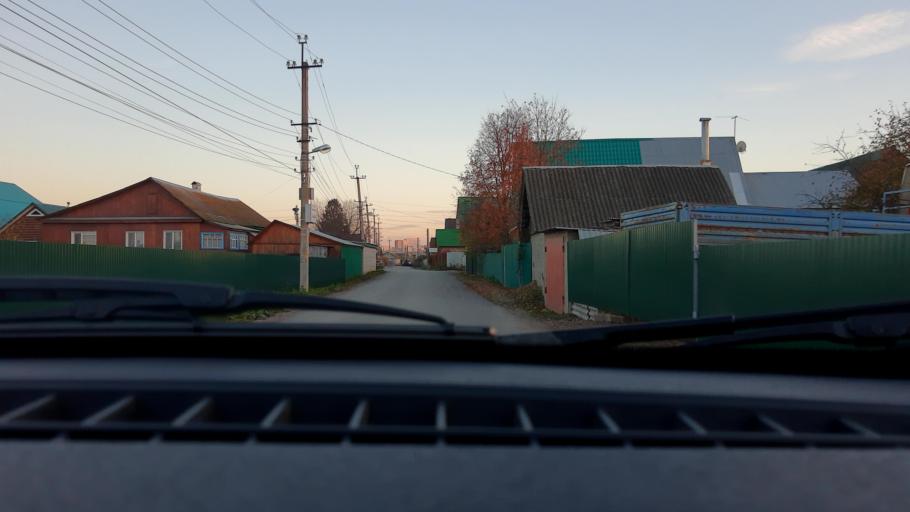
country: RU
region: Bashkortostan
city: Mikhaylovka
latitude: 54.7618
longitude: 55.9042
